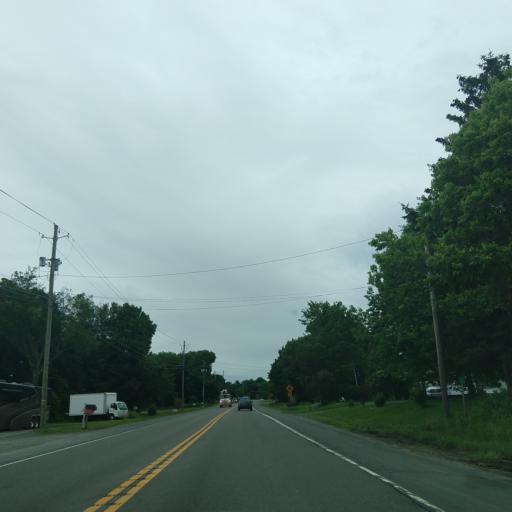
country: US
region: New York
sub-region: Tompkins County
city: Dryden
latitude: 42.4863
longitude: -76.3482
